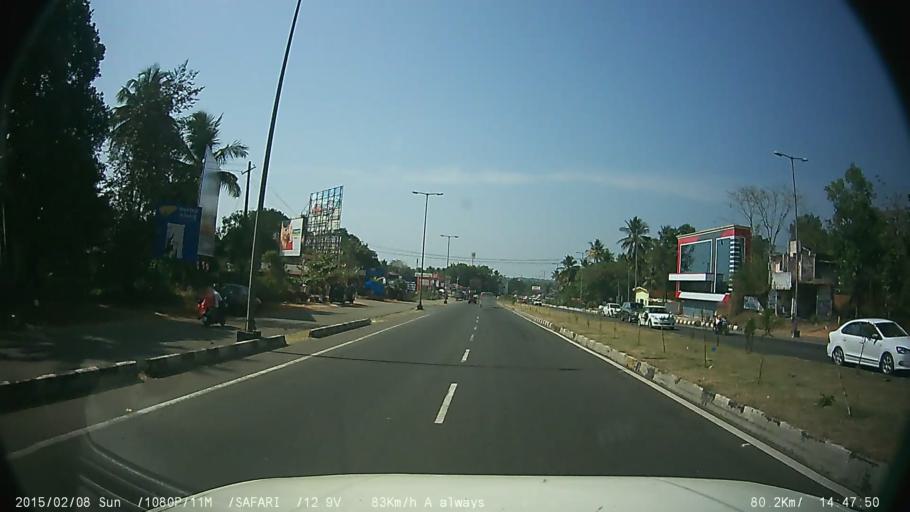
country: IN
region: Kerala
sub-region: Ernakulam
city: Angamali
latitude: 10.2440
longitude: 76.3721
